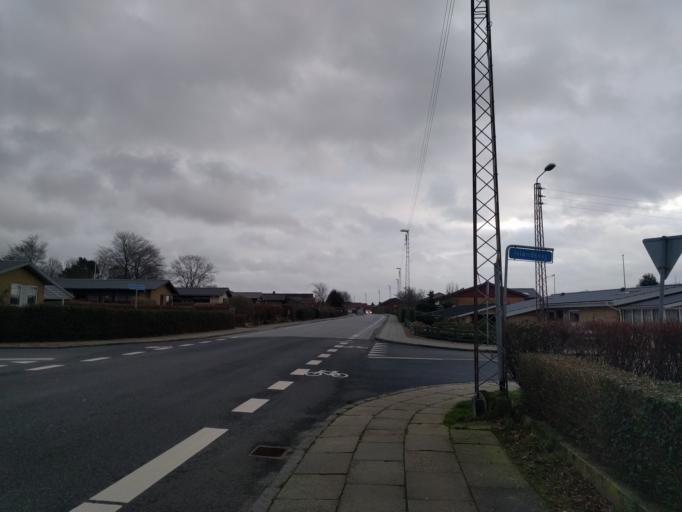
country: DK
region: Central Jutland
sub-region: Viborg Kommune
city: Viborg
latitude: 56.4562
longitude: 9.3805
